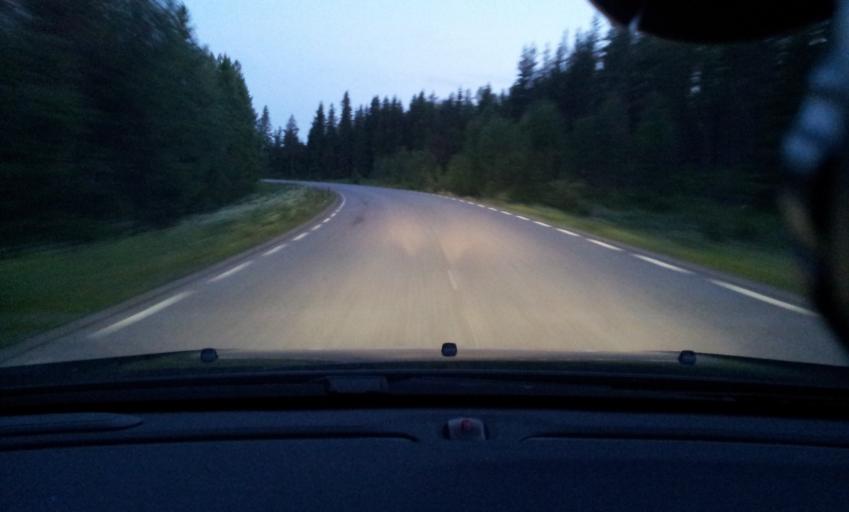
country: SE
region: Jaemtland
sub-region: Braecke Kommun
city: Braecke
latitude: 62.7560
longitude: 15.2819
